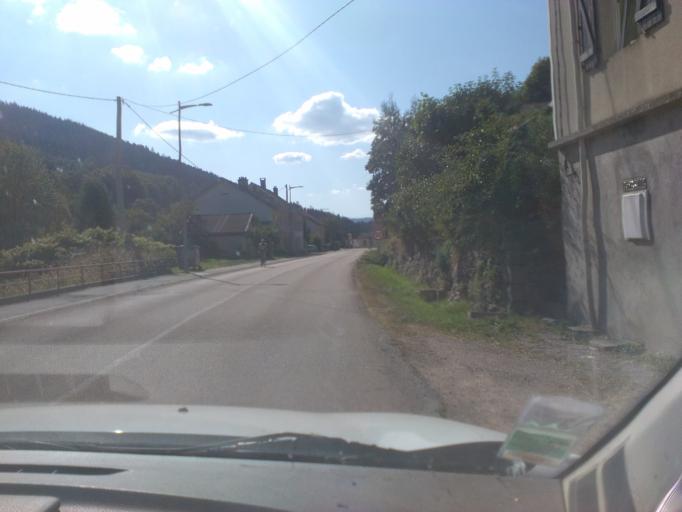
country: FR
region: Lorraine
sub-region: Departement des Vosges
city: Cornimont
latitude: 48.0234
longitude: 6.7904
